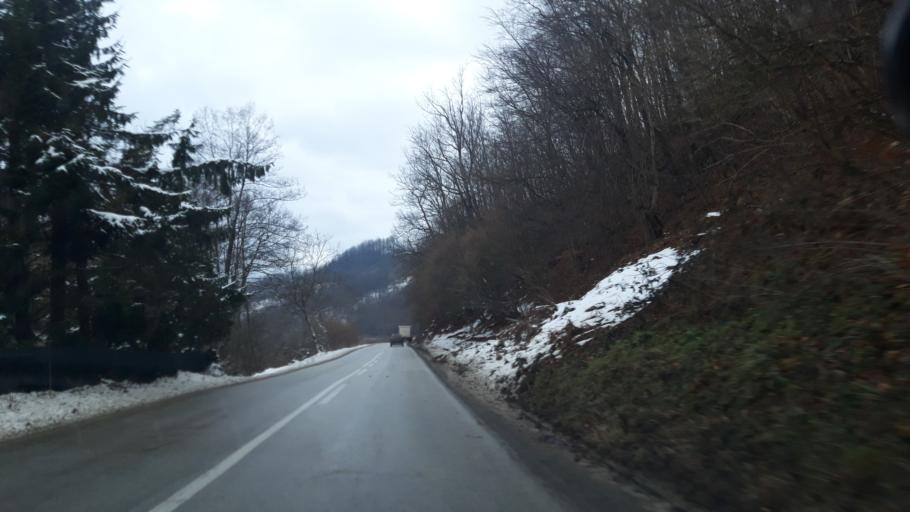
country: BA
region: Republika Srpska
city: Vlasenica
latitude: 44.1845
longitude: 18.9919
